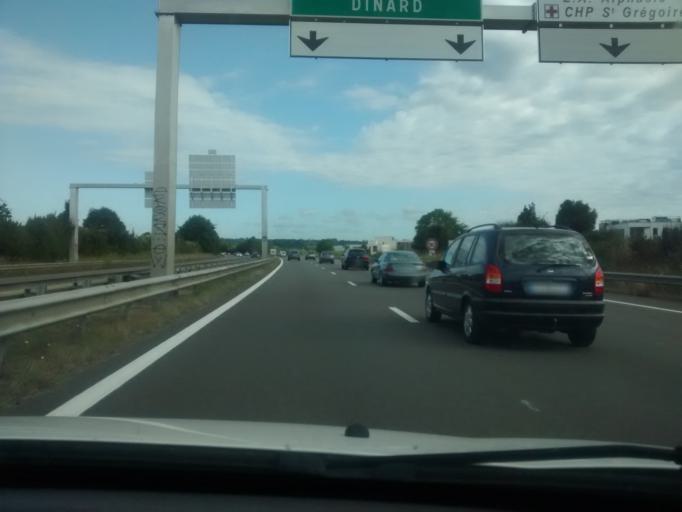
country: FR
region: Brittany
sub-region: Departement d'Ille-et-Vilaine
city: Saint-Gregoire
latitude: 48.1490
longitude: -1.6992
